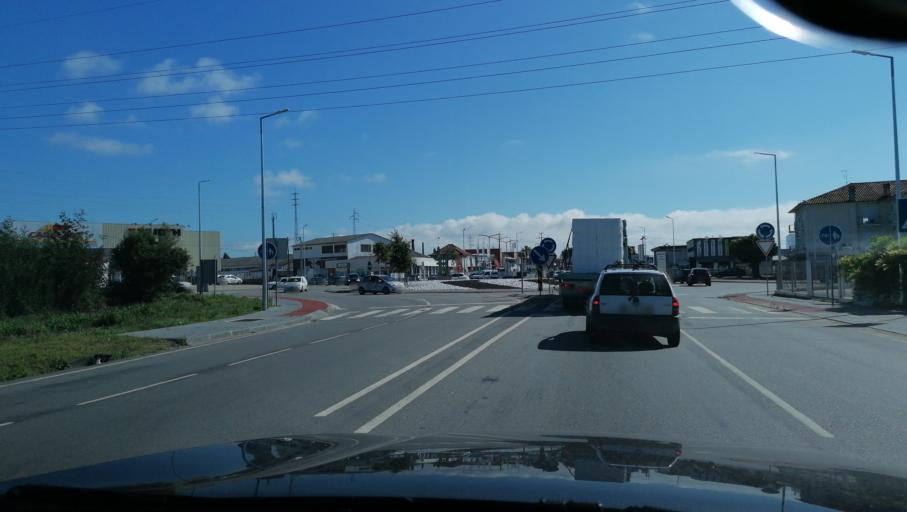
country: PT
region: Aveiro
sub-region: Aveiro
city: Aveiro
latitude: 40.6644
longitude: -8.6110
